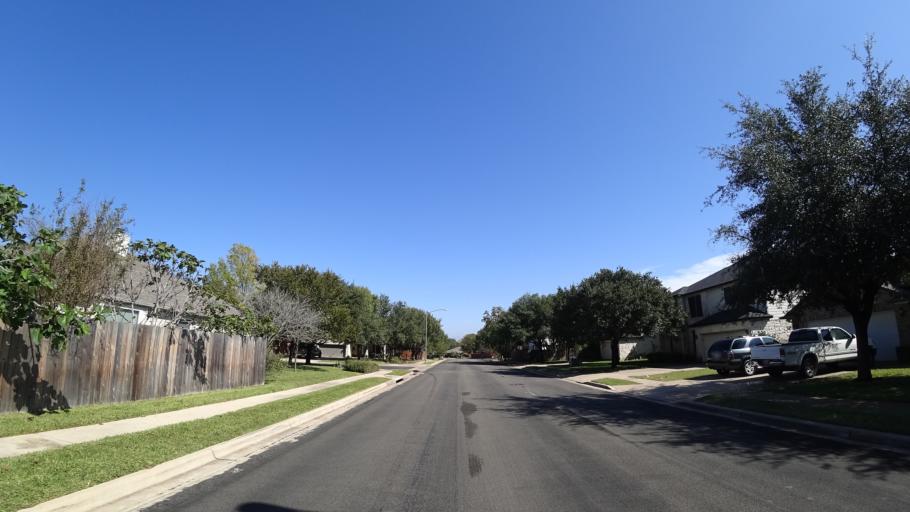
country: US
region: Texas
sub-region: Travis County
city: Shady Hollow
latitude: 30.1950
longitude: -97.8632
